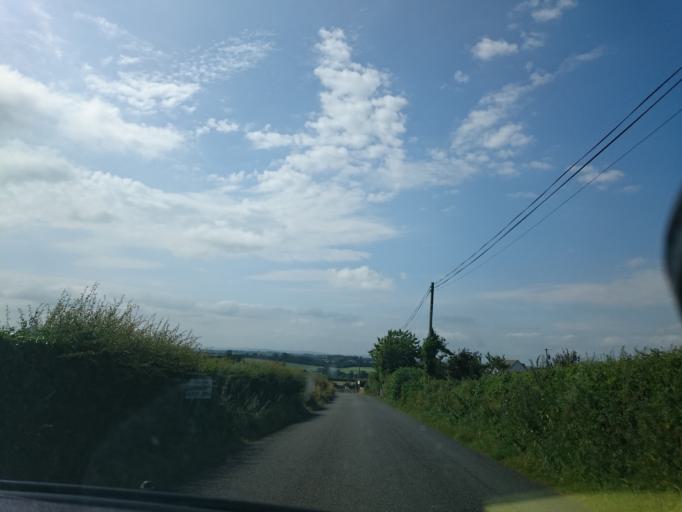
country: IE
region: Leinster
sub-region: Kilkenny
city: Thomastown
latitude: 52.5323
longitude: -7.2186
